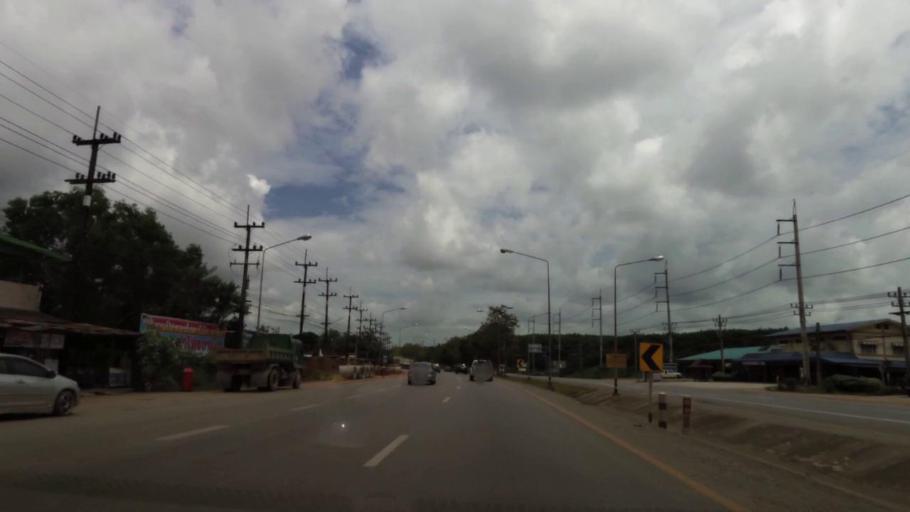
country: TH
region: Chanthaburi
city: Na Yai Am
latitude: 12.7872
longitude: 101.7891
